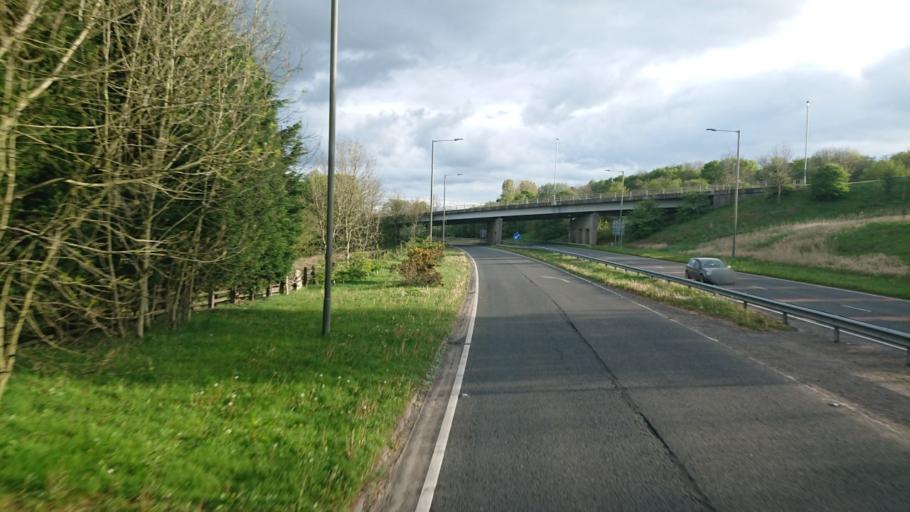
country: GB
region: England
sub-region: Lancashire
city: Haslingden
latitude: 53.6937
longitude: -2.3056
